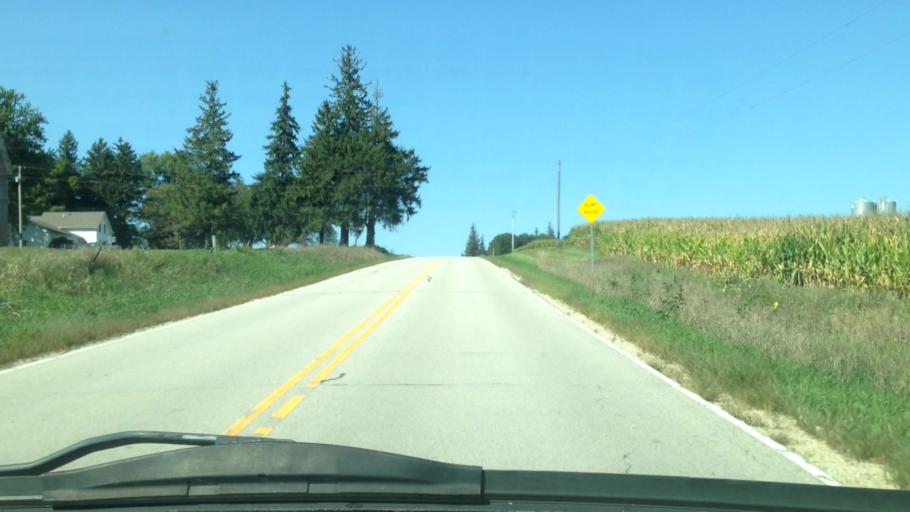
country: US
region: Minnesota
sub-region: Fillmore County
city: Rushford
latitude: 43.7029
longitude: -91.7703
